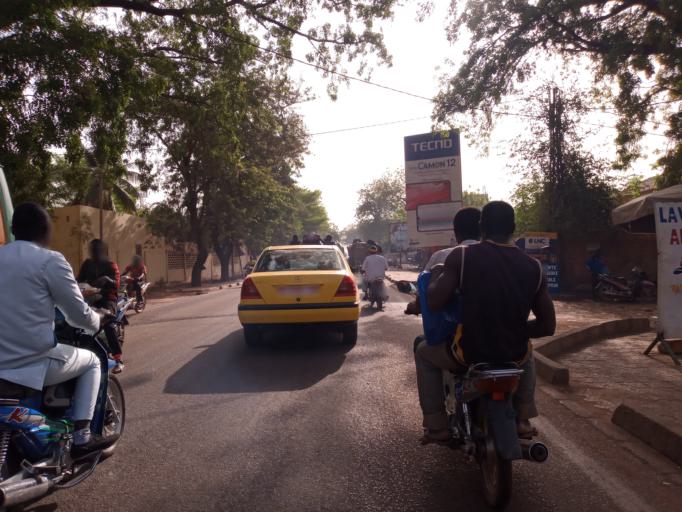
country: ML
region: Bamako
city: Bamako
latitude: 12.6578
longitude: -7.9966
